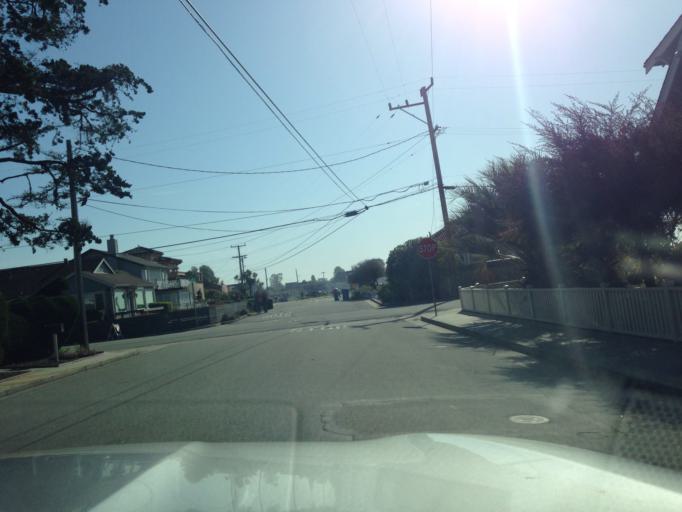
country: US
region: California
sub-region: Santa Cruz County
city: Santa Cruz
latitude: 36.9529
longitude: -122.0426
